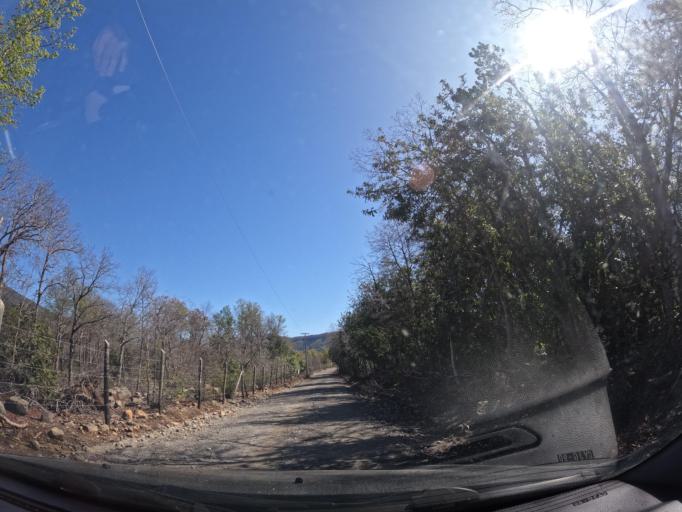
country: CL
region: Maule
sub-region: Provincia de Linares
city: Longavi
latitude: -36.2394
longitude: -71.3540
